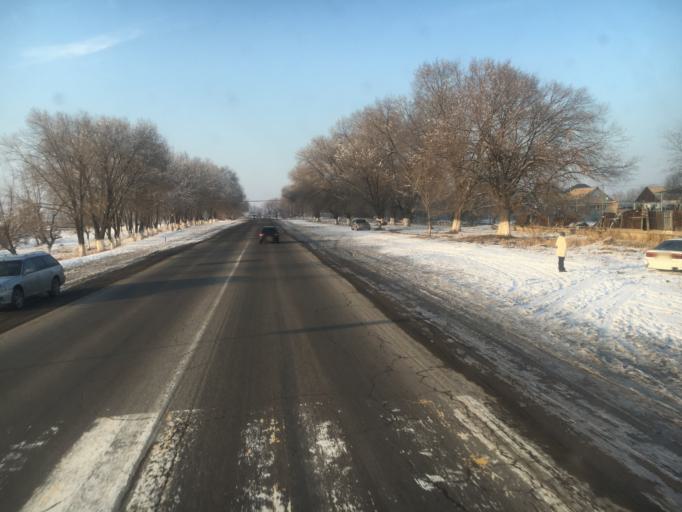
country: KZ
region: Almaty Oblysy
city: Burunday
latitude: 43.3376
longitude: 76.6596
